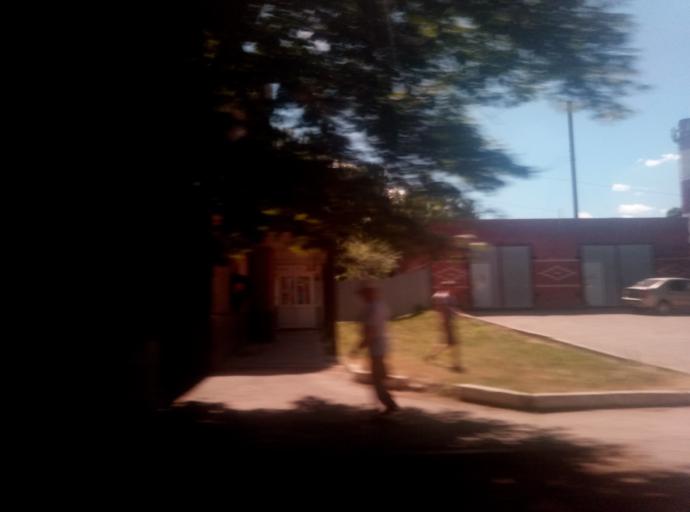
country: RU
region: Tula
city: Kireyevsk
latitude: 53.9289
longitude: 37.9270
